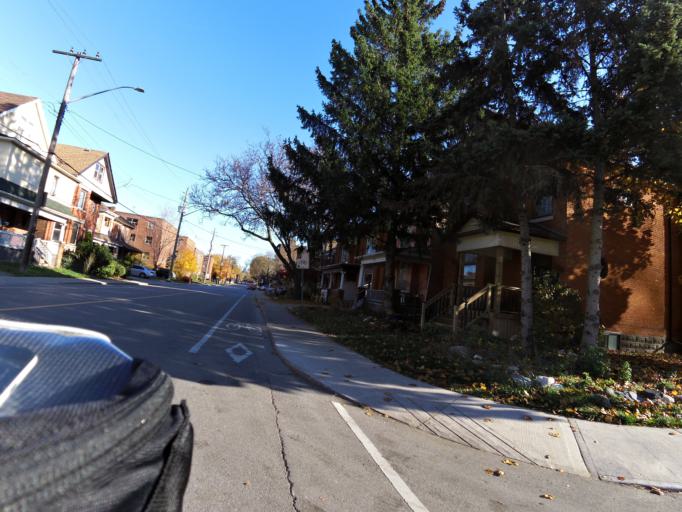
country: CA
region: Ontario
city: Hamilton
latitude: 43.2484
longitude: -79.8562
